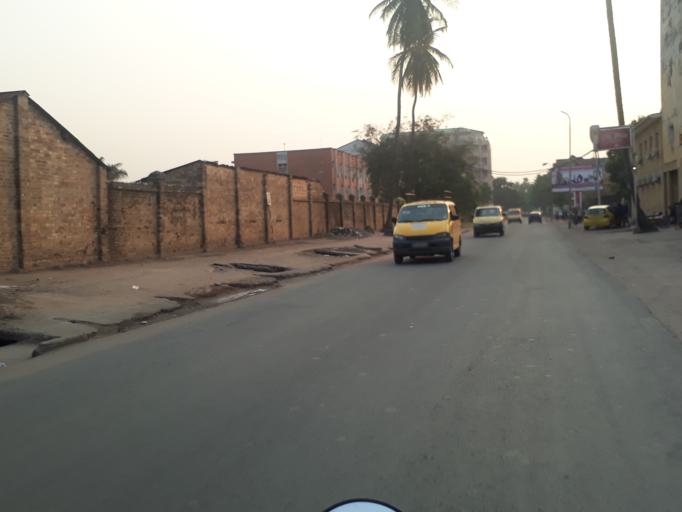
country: CD
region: Kinshasa
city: Kinshasa
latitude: -4.3071
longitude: 15.3045
